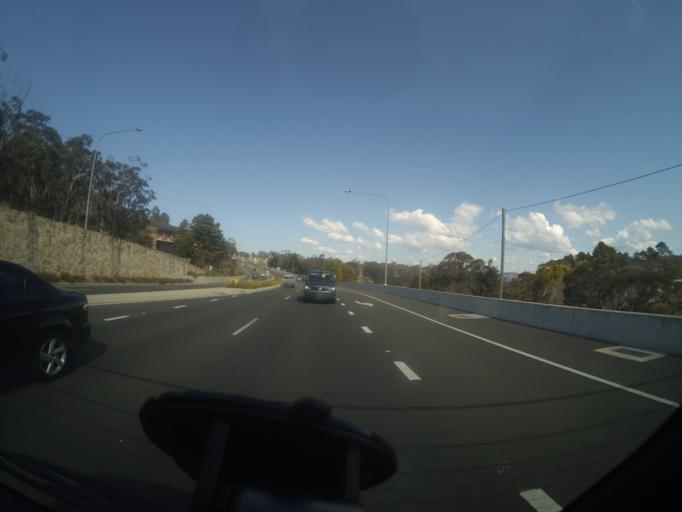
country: AU
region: New South Wales
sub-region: Blue Mountains Municipality
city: Lawson
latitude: -33.7177
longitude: 150.3827
